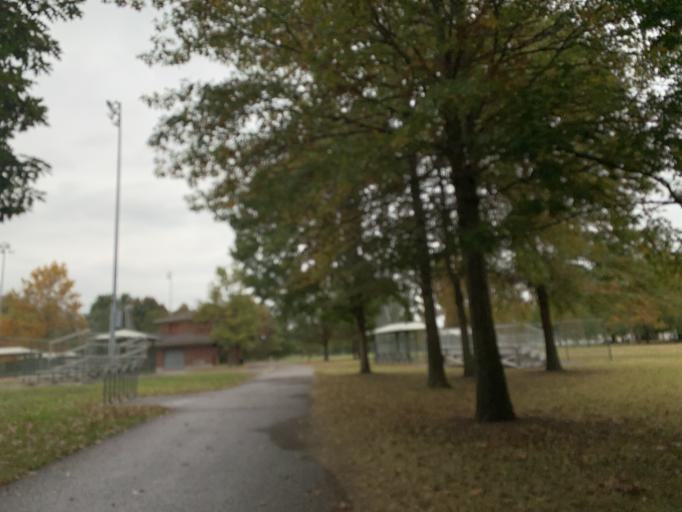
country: US
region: Indiana
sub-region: Floyd County
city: New Albany
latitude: 38.2622
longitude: -85.8281
